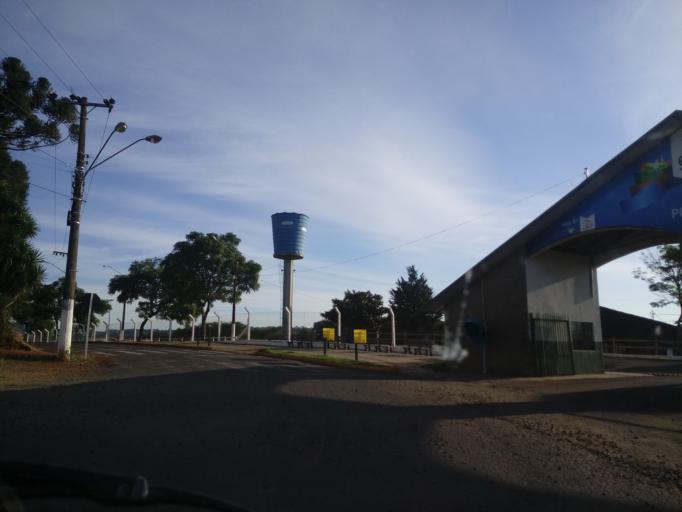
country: BR
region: Santa Catarina
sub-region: Chapeco
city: Chapeco
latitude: -27.0947
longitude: -52.6623
